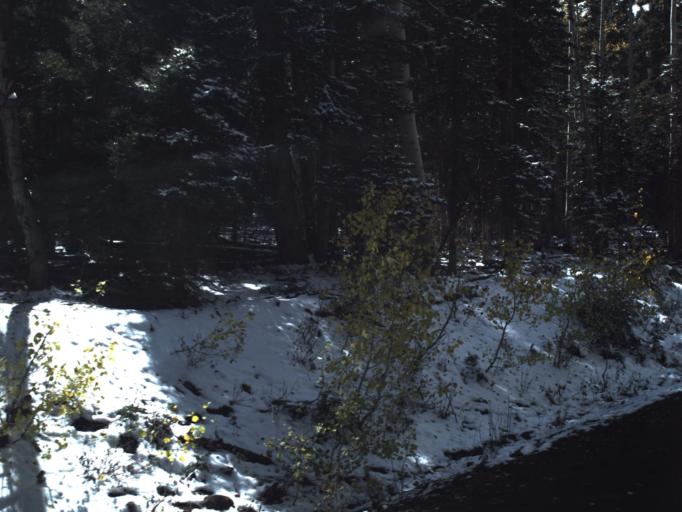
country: US
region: Utah
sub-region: Piute County
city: Junction
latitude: 38.2422
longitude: -112.3508
